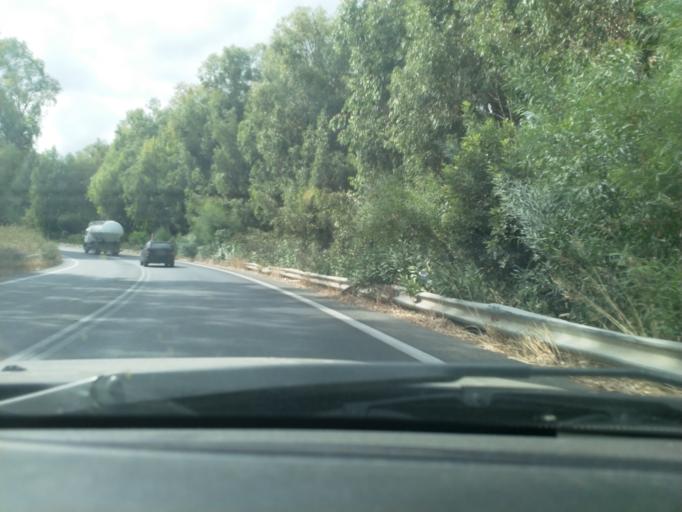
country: GR
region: Crete
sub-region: Nomos Chanias
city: Georgioupolis
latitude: 35.3619
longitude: 24.2566
